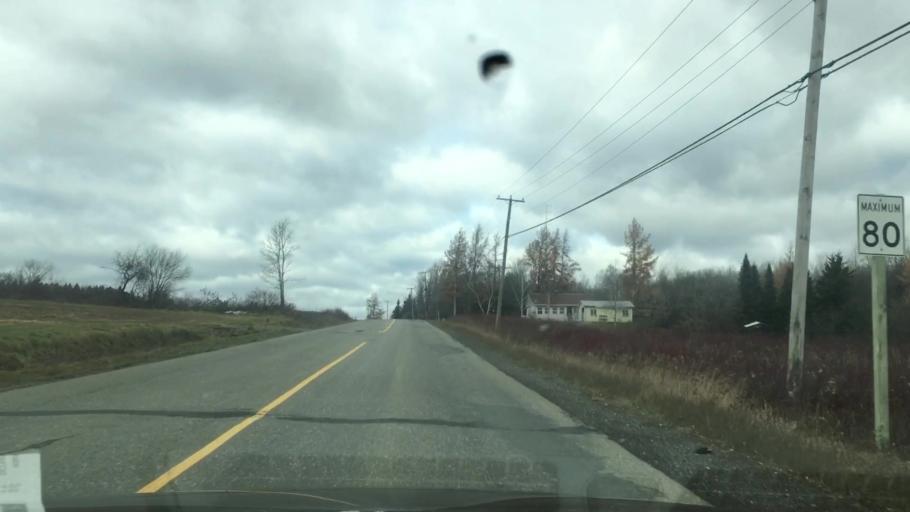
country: US
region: Maine
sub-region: Aroostook County
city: Fort Fairfield
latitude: 46.7530
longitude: -67.7584
